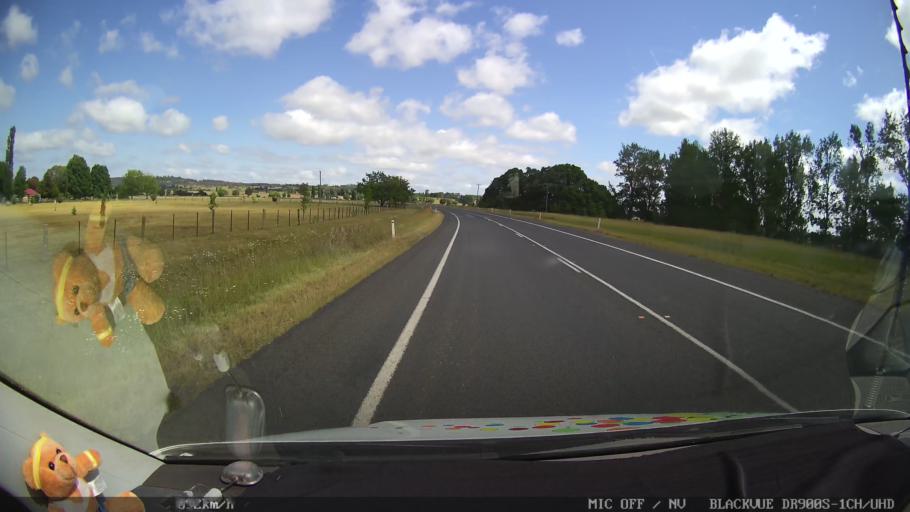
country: AU
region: New South Wales
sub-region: Glen Innes Severn
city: Glen Innes
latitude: -29.8116
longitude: 151.7412
